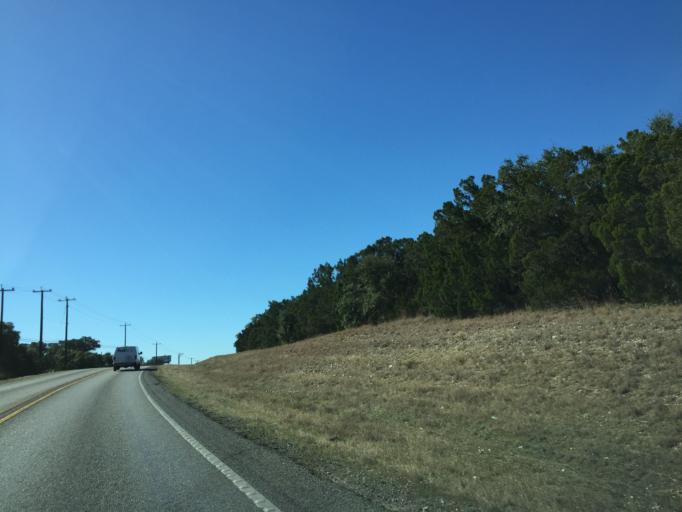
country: US
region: Texas
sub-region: Comal County
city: Garden Ridge
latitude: 29.7109
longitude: -98.3100
